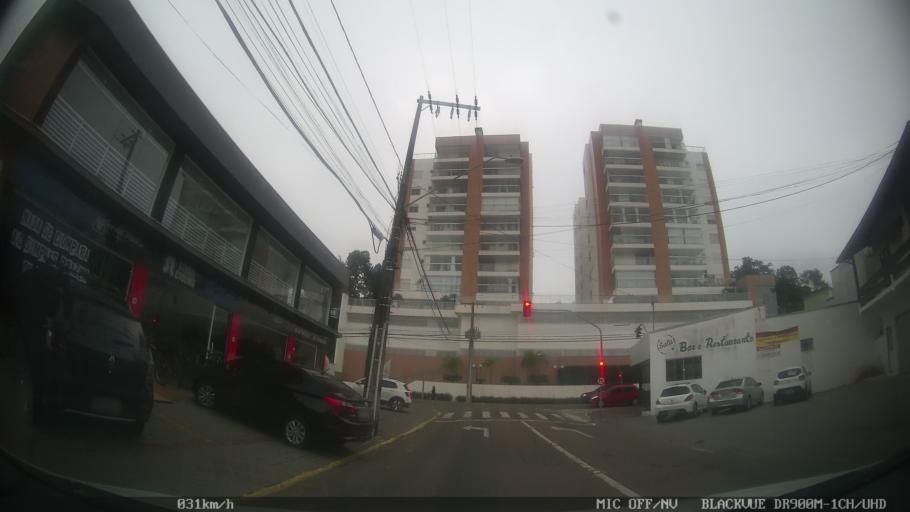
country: BR
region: Santa Catarina
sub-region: Joinville
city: Joinville
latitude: -26.2825
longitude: -48.8391
